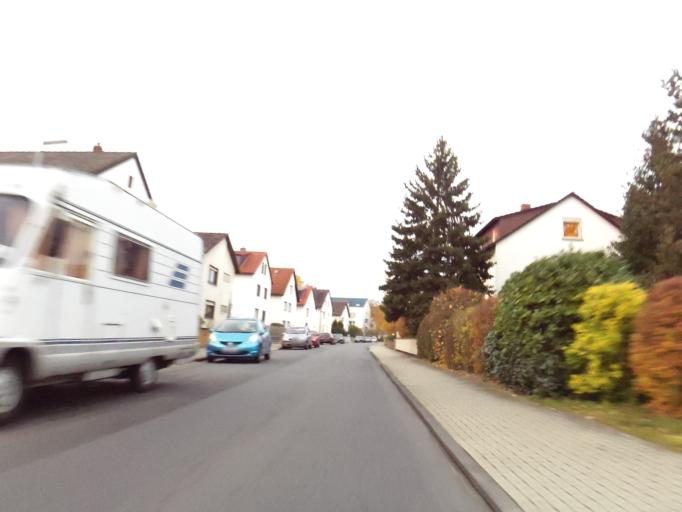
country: DE
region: Hesse
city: Morfelden-Walldorf
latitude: 49.9739
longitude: 8.5592
